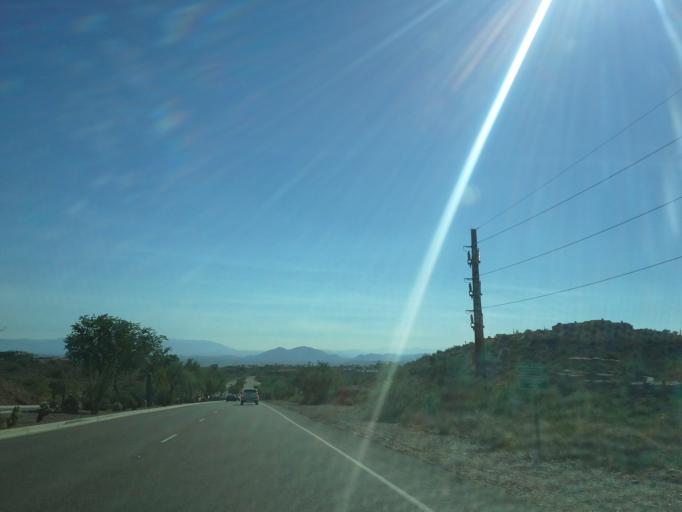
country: US
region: Arizona
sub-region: Maricopa County
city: Fountain Hills
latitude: 33.5811
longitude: -111.7498
